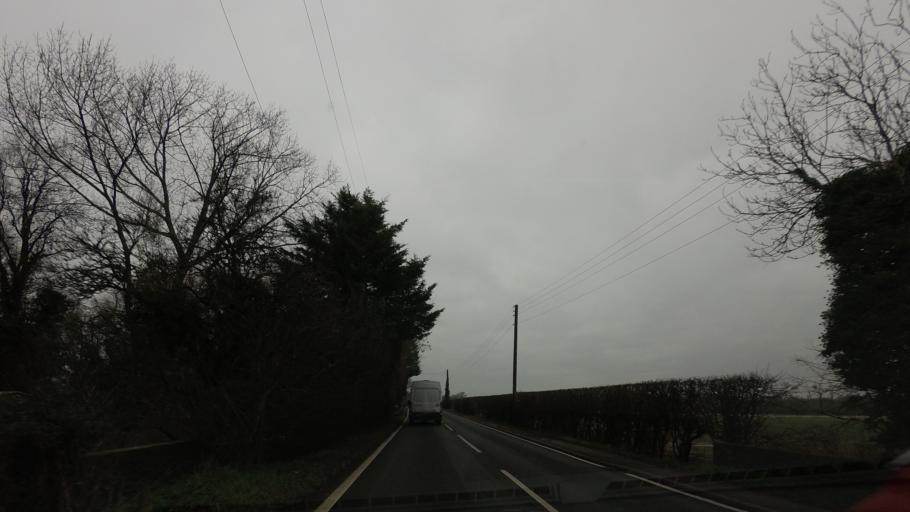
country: GB
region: England
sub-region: Kent
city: Staplehurst
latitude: 51.1407
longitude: 0.5532
